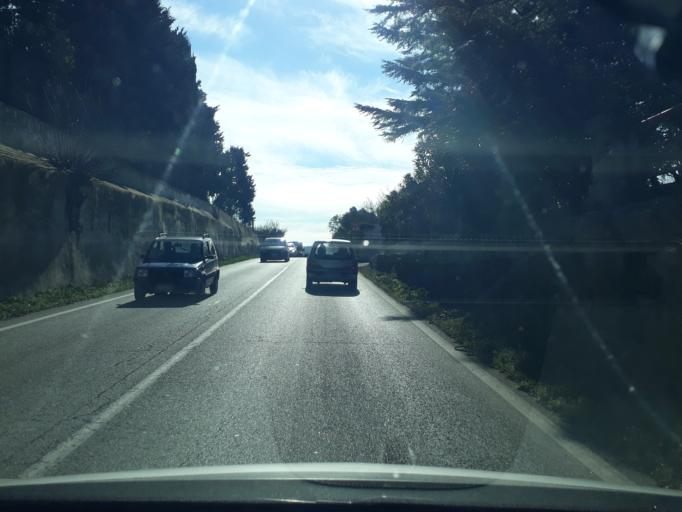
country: IT
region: Apulia
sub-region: Provincia di Bari
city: Locorotondo
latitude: 40.7303
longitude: 17.3326
